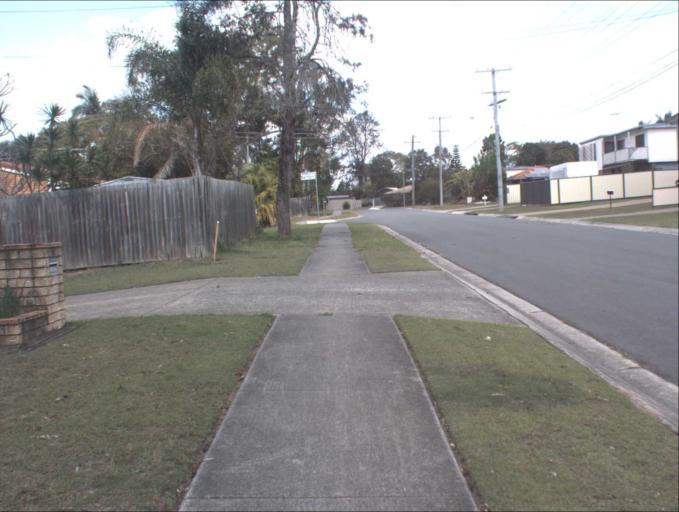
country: AU
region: Queensland
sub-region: Logan
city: Logan Reserve
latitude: -27.6834
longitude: 153.0864
